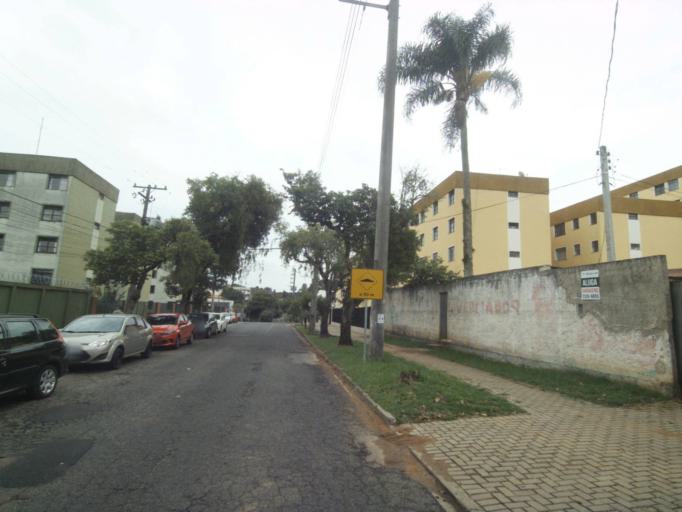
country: BR
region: Parana
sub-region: Curitiba
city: Curitiba
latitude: -25.4172
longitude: -49.2911
